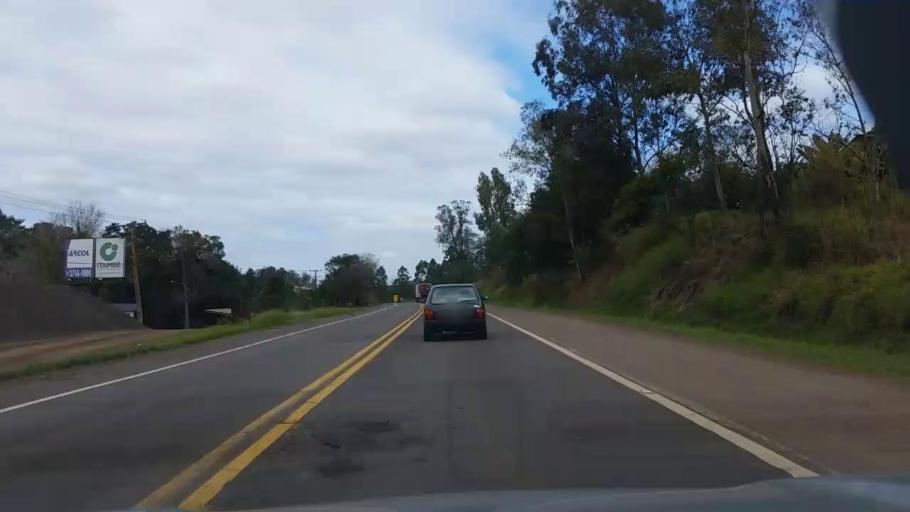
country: BR
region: Rio Grande do Sul
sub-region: Lajeado
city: Lajeado
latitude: -29.4233
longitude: -52.0214
